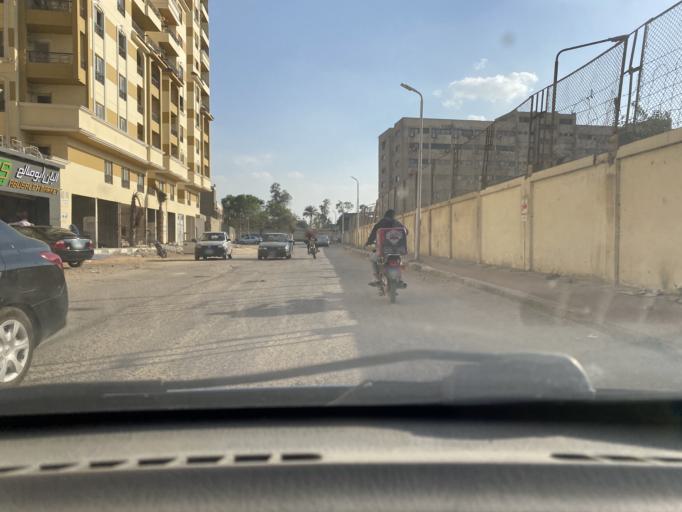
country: EG
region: Muhafazat al Qahirah
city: Cairo
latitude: 30.1038
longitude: 31.3040
